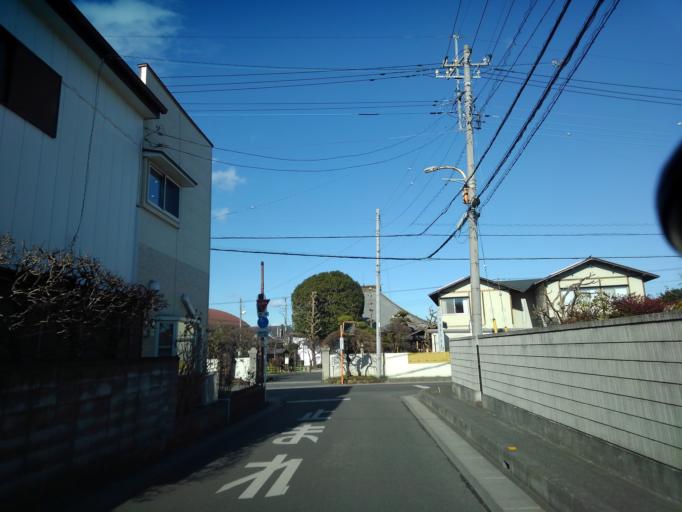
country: JP
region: Saitama
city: Sayama
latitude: 35.7918
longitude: 139.3799
